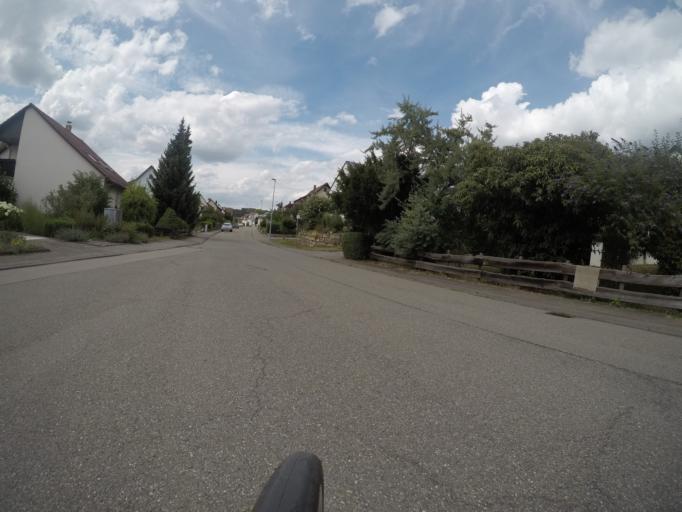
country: DE
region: Baden-Wuerttemberg
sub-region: Regierungsbezirk Stuttgart
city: Weil der Stadt
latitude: 48.7216
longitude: 8.8954
